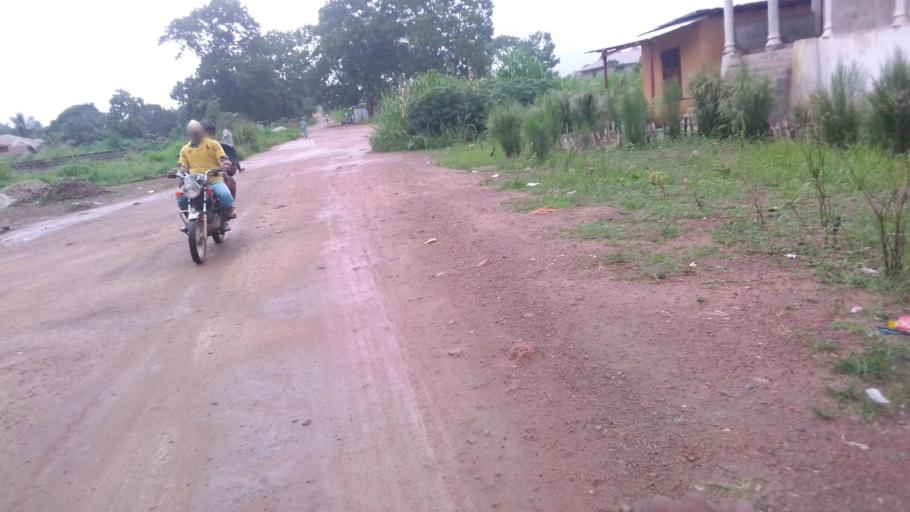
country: SL
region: Eastern Province
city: Kenema
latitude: 7.8996
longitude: -11.1701
